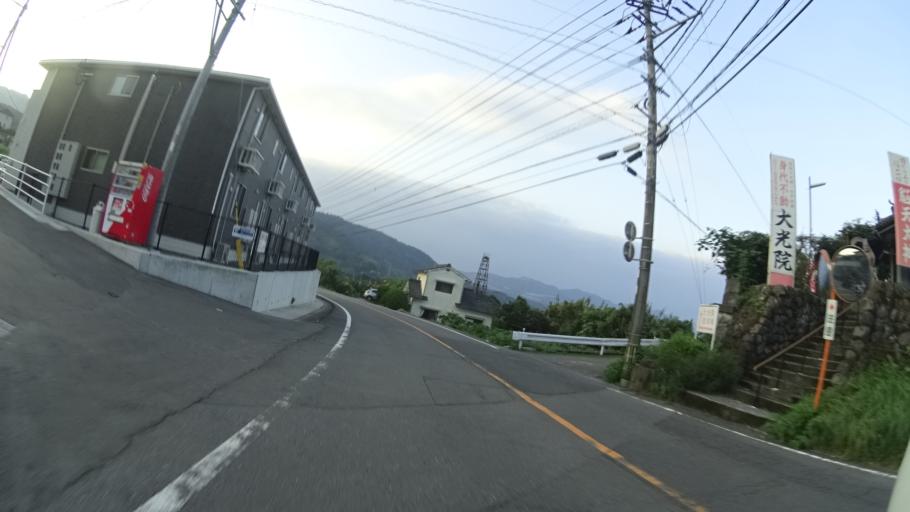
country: JP
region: Oita
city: Beppu
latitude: 33.3199
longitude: 131.4809
